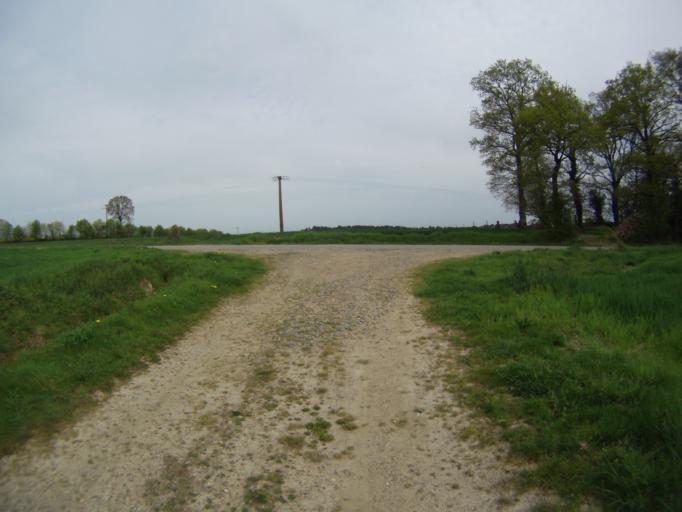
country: FR
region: Brittany
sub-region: Departement d'Ille-et-Vilaine
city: Chanteloup
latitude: 47.9382
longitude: -1.6220
